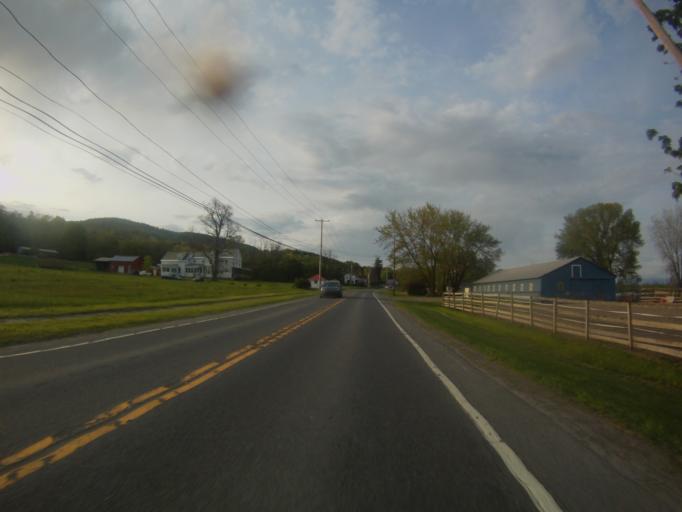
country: US
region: New York
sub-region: Essex County
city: Ticonderoga
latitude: 43.8821
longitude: -73.4491
